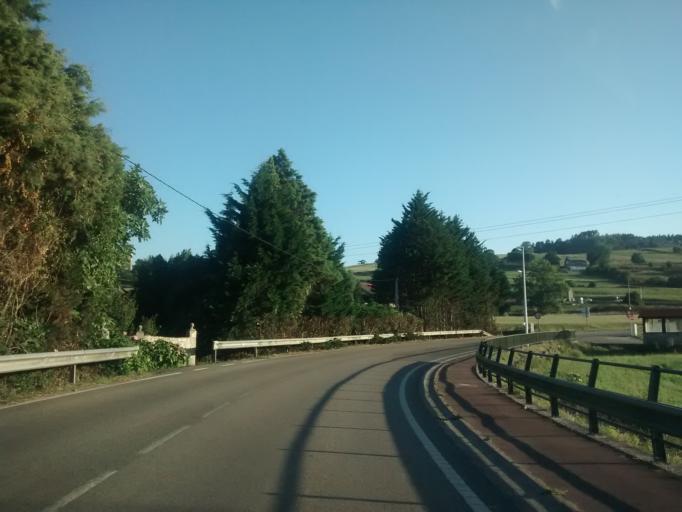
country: ES
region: Cantabria
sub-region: Provincia de Cantabria
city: San Miguel de Meruelo
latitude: 43.4500
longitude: -3.5721
